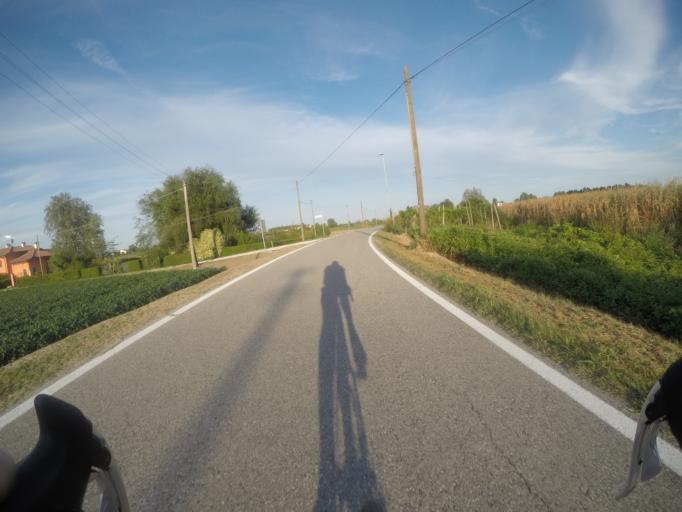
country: IT
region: Veneto
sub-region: Provincia di Rovigo
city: San Bellino
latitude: 45.0190
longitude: 11.5655
